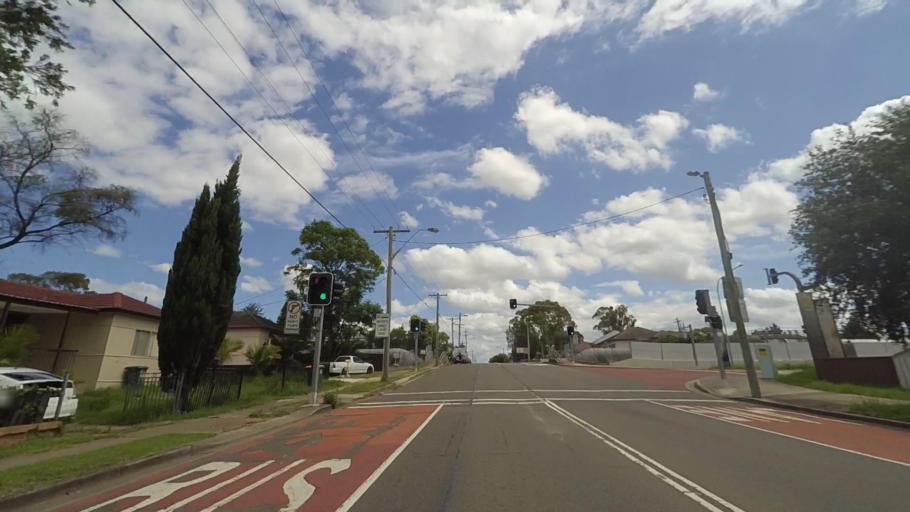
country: AU
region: New South Wales
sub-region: Holroyd
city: Guildford West
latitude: -33.8444
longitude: 150.9628
